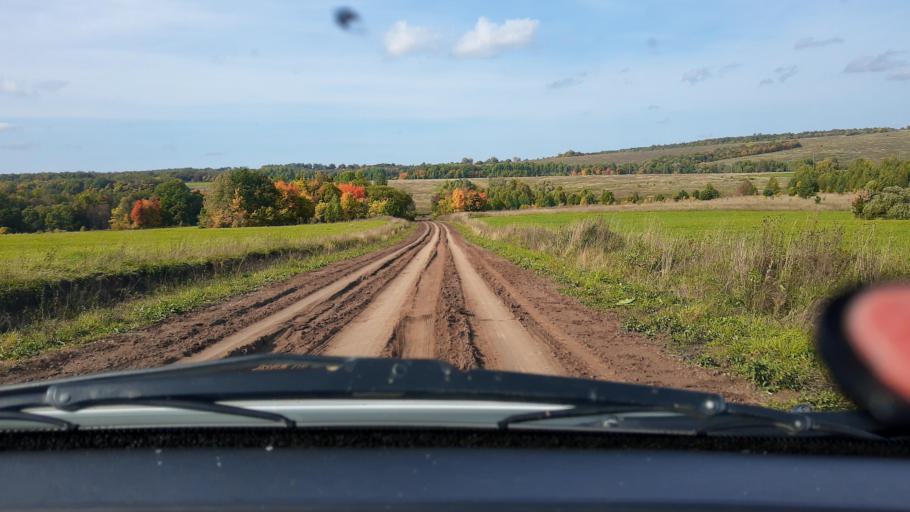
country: RU
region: Bashkortostan
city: Kudeyevskiy
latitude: 54.7135
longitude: 56.6382
